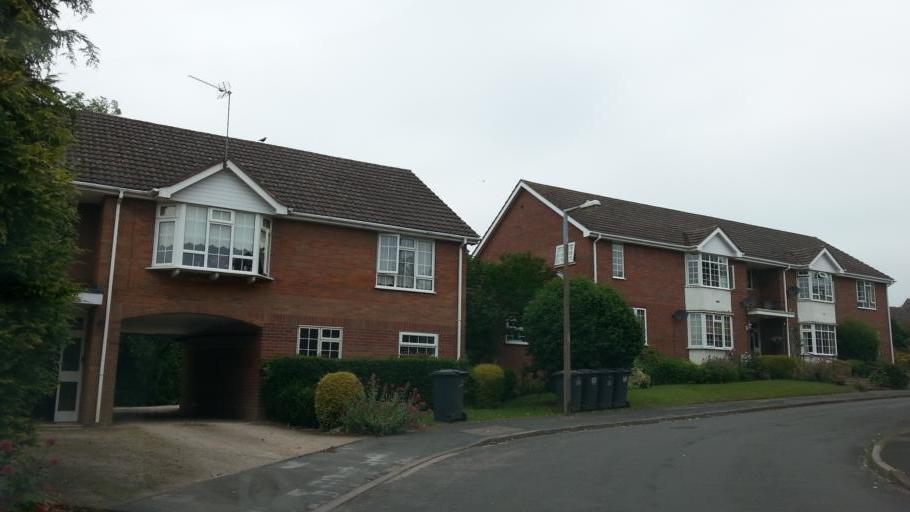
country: GB
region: England
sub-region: Staffordshire
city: Armitage
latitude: 52.8202
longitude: -1.8855
